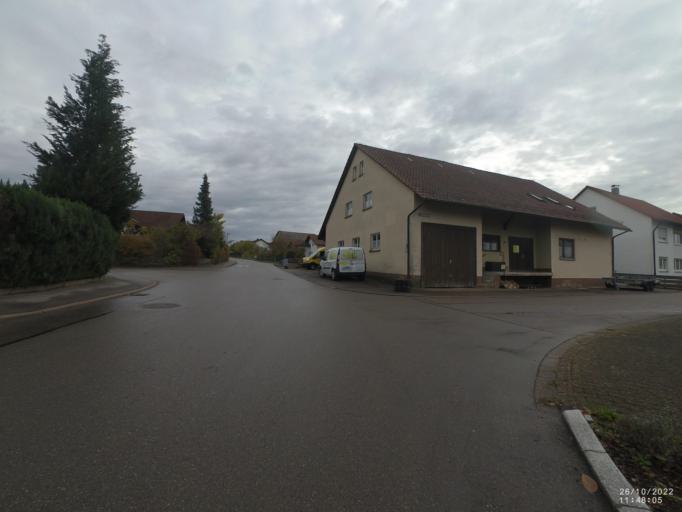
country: DE
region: Baden-Wuerttemberg
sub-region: Regierungsbezirk Stuttgart
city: Bohmenkirch
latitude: 48.6917
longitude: 9.8946
